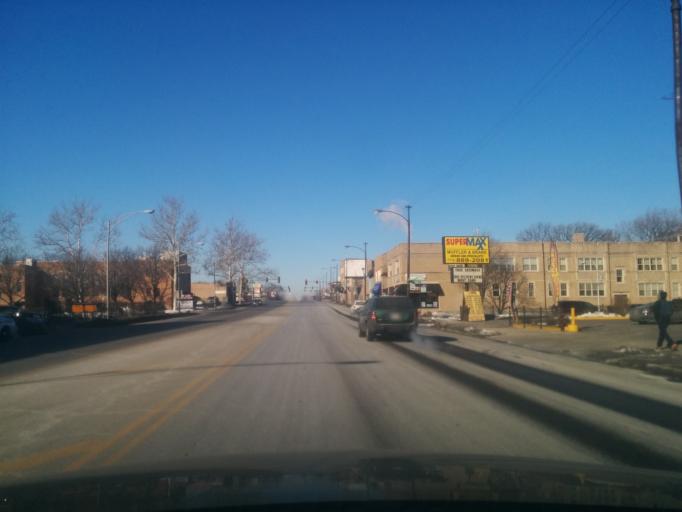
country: US
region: Illinois
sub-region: Cook County
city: Oak Park
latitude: 41.9092
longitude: -87.7810
